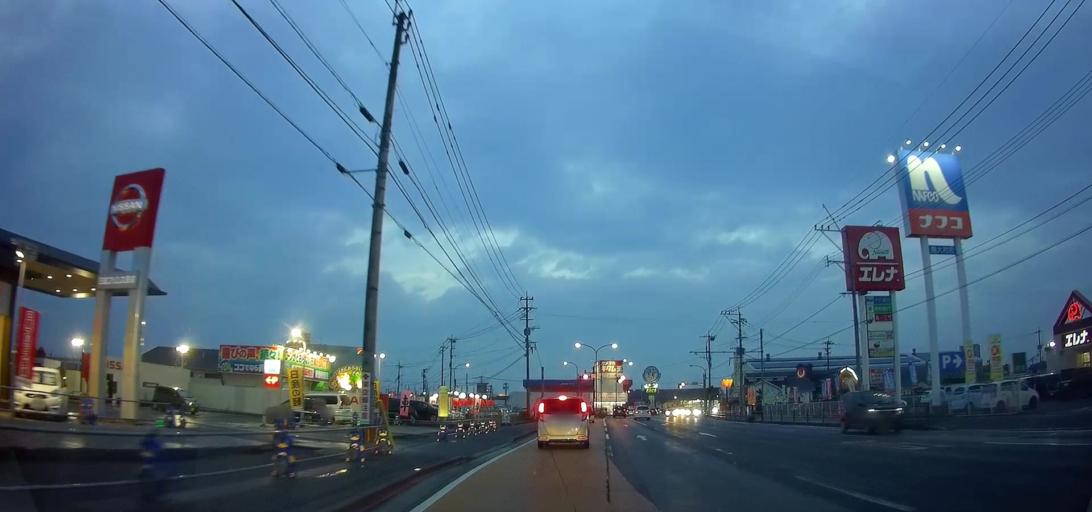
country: JP
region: Nagasaki
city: Omura
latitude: 32.9113
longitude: 129.9519
